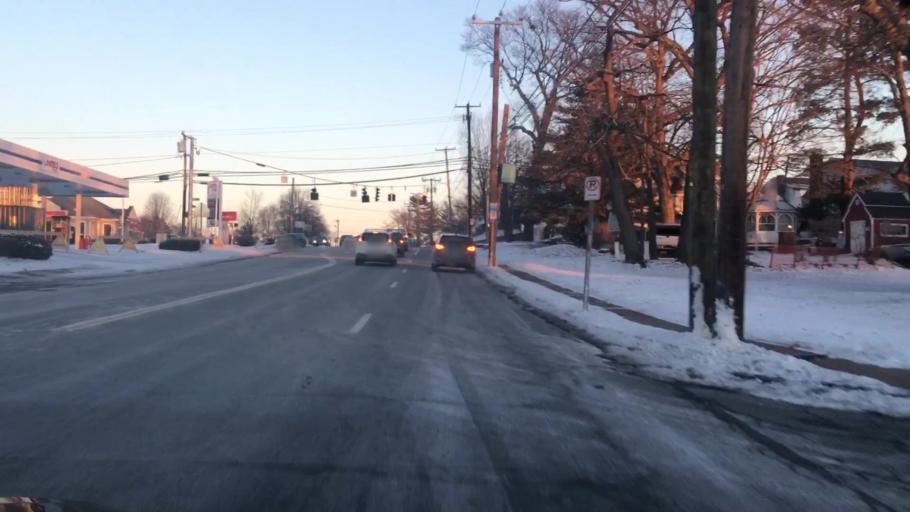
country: US
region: Connecticut
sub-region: Hartford County
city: Manchester
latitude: 41.7811
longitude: -72.5508
